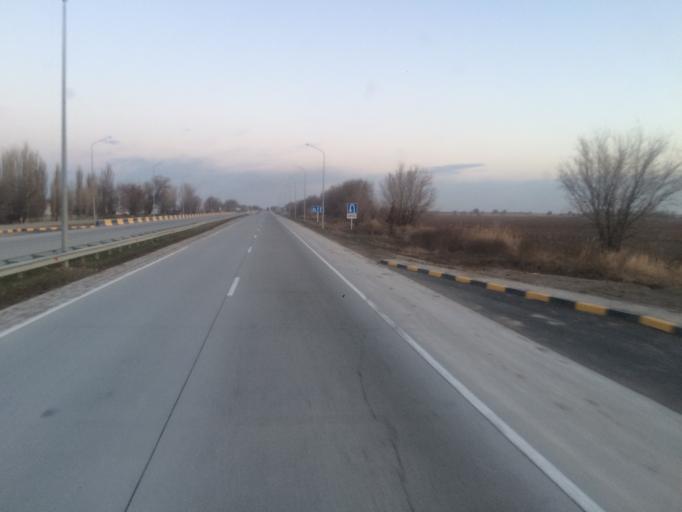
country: KZ
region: Ongtustik Qazaqstan
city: Shayan
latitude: 42.9592
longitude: 68.8904
